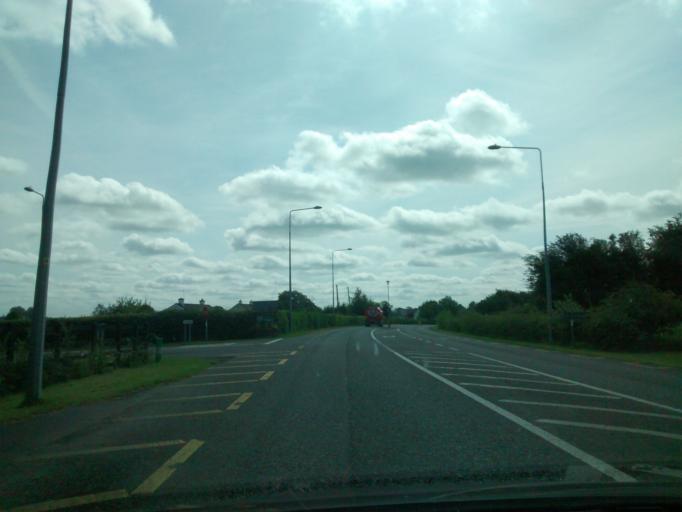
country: IE
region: Leinster
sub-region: An Iarmhi
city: Moate
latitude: 53.3800
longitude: -7.6657
